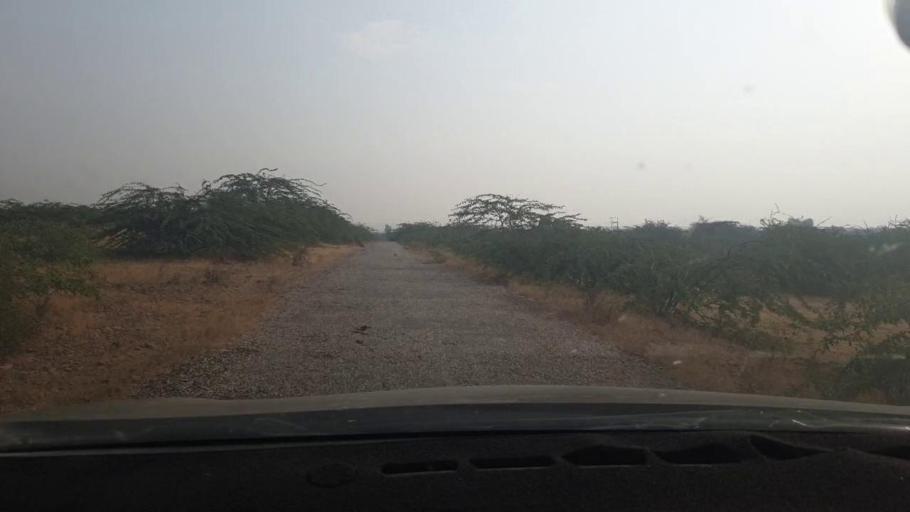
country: PK
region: Sindh
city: Malir Cantonment
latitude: 24.9561
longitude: 67.4526
